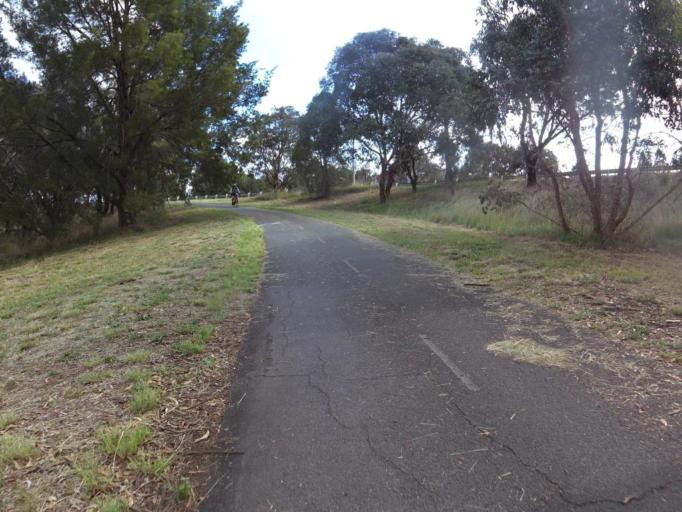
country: AU
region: Australian Capital Territory
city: Belconnen
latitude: -35.2277
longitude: 149.0762
